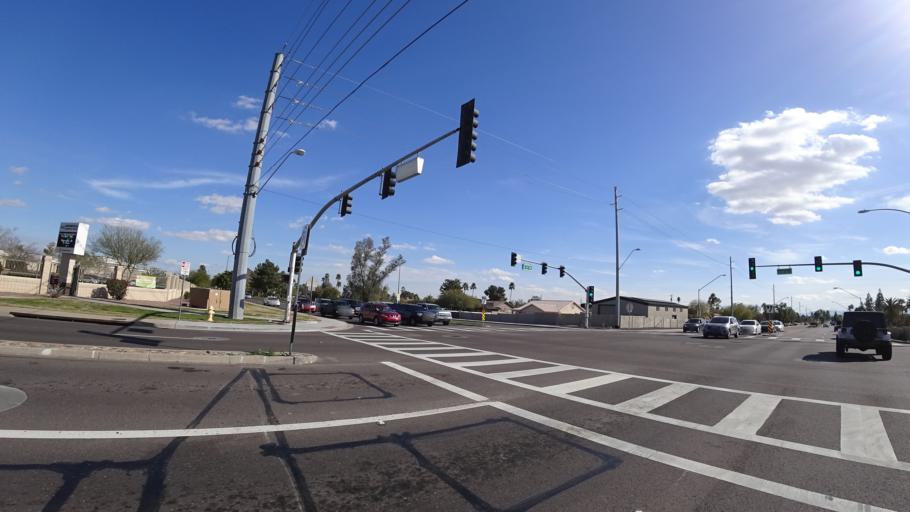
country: US
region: Arizona
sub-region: Maricopa County
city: Peoria
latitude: 33.6529
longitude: -112.2205
